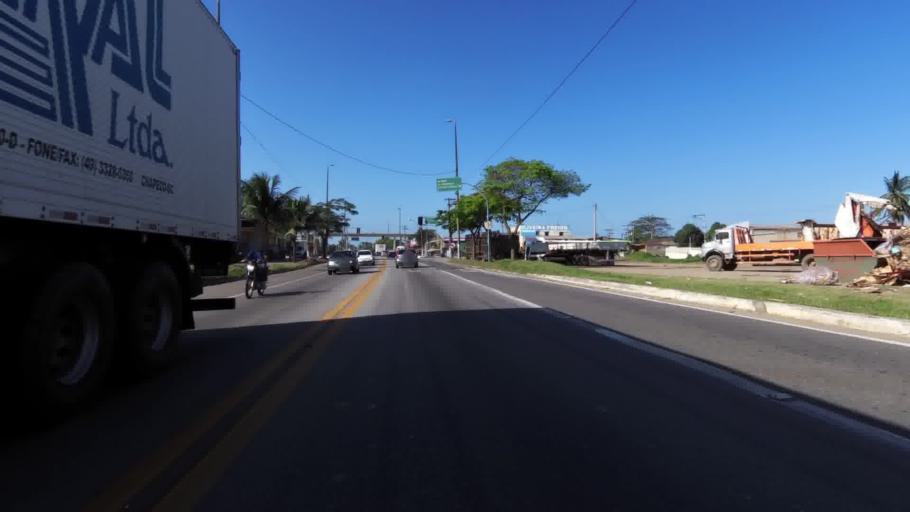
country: BR
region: Rio de Janeiro
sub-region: Campos Dos Goytacazes
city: Campos
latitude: -21.7197
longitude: -41.3135
